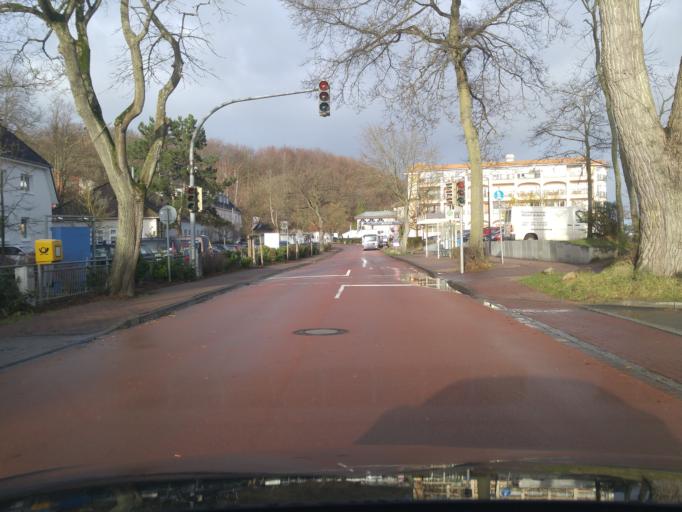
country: DE
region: Schleswig-Holstein
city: Timmendorfer Strand
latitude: 54.0087
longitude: 10.7711
